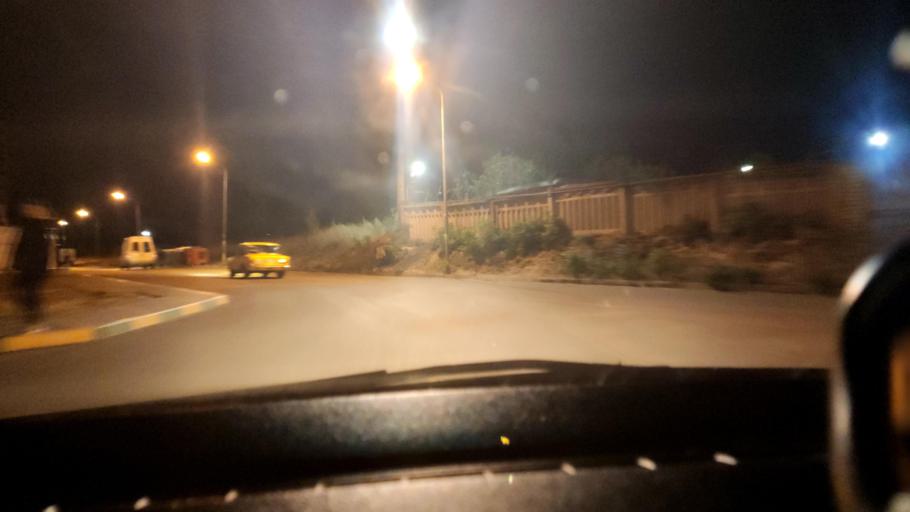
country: RU
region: Voronezj
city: Shilovo
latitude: 51.5713
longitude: 39.1272
